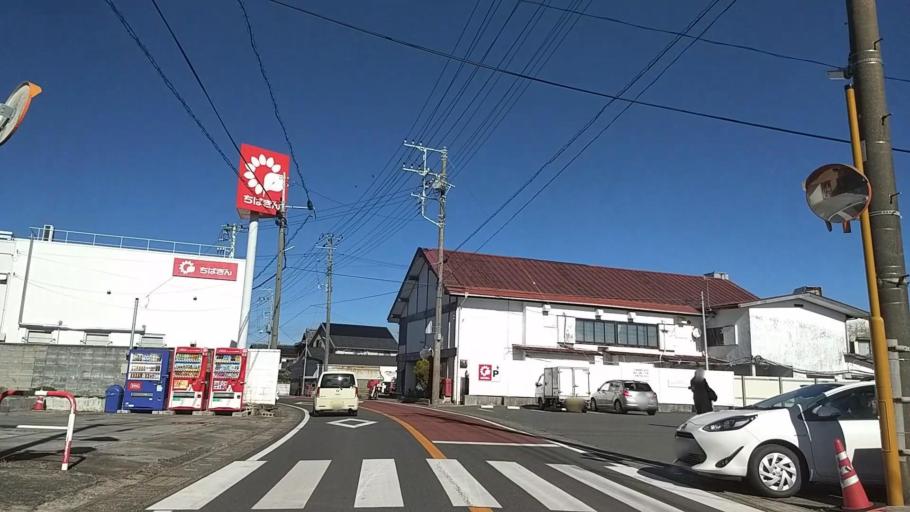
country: JP
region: Chiba
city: Tateyama
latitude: 34.9590
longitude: 139.9593
